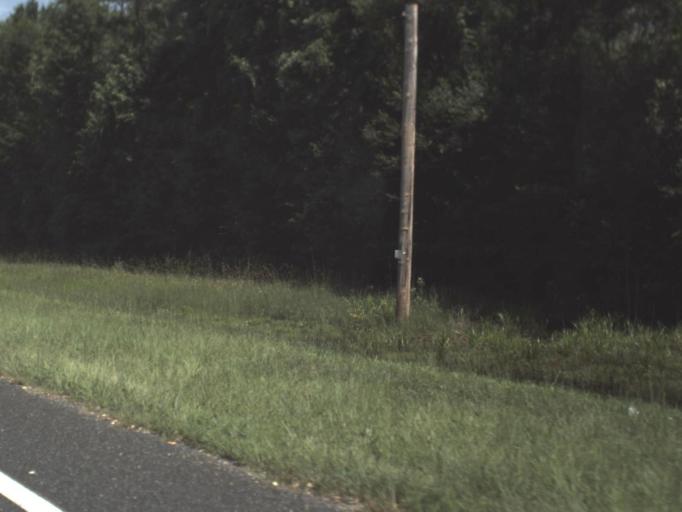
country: US
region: Florida
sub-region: Dixie County
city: Cross City
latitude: 29.6589
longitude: -83.1914
